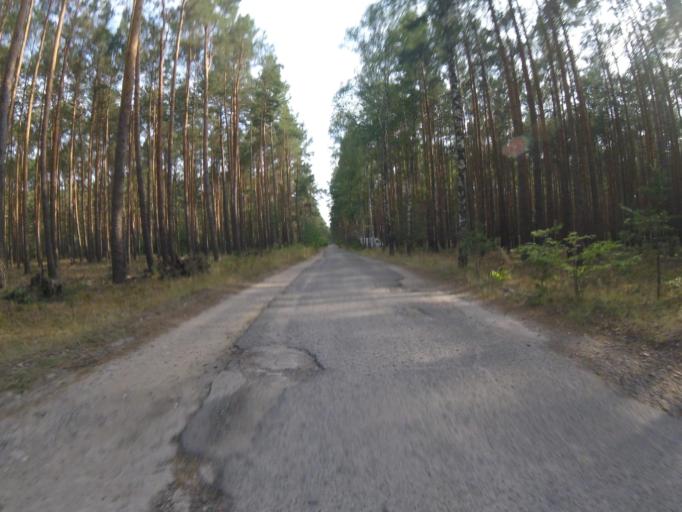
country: DE
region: Brandenburg
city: Gross Koris
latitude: 52.2176
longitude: 13.7400
